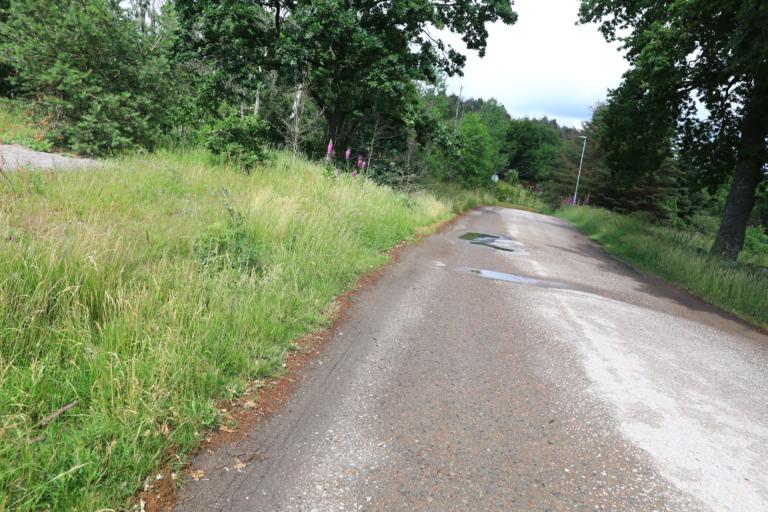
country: SE
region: Halland
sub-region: Varbergs Kommun
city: Varberg
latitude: 57.1730
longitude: 12.2900
